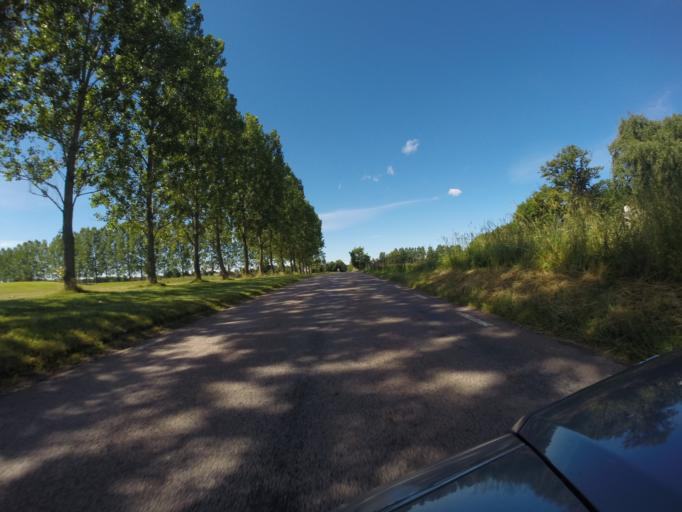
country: SE
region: Skane
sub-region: Helsingborg
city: Odakra
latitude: 56.1275
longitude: 12.7007
